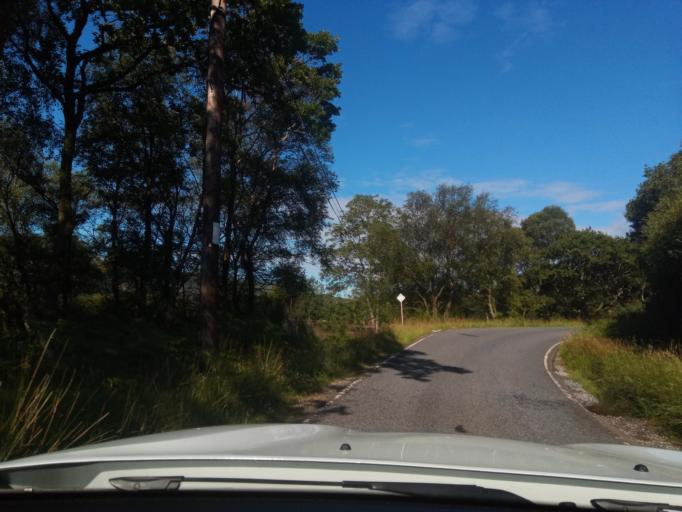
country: GB
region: Scotland
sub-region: Argyll and Bute
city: Isle Of Mull
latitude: 56.6889
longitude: -5.6671
